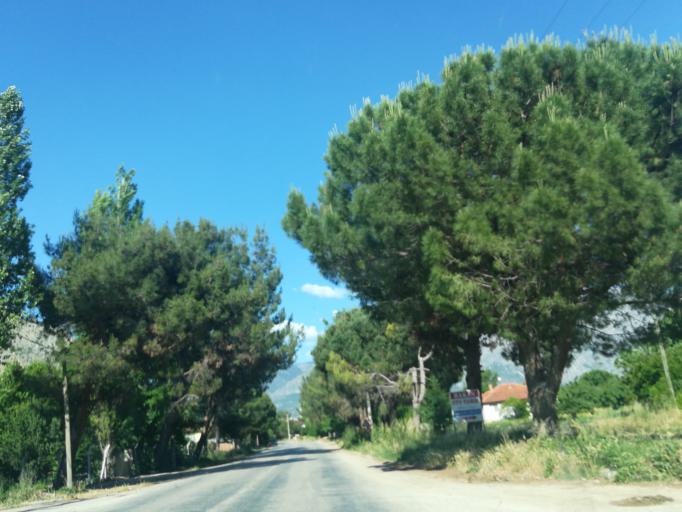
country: TR
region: Denizli
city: Civril
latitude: 38.3198
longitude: 29.8369
